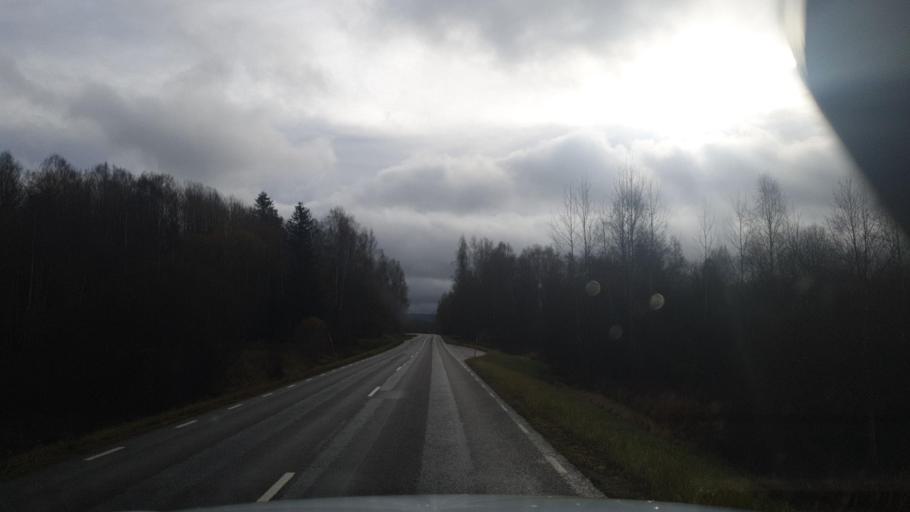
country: SE
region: Vaermland
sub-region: Eda Kommun
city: Amotfors
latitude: 59.6885
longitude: 12.0958
